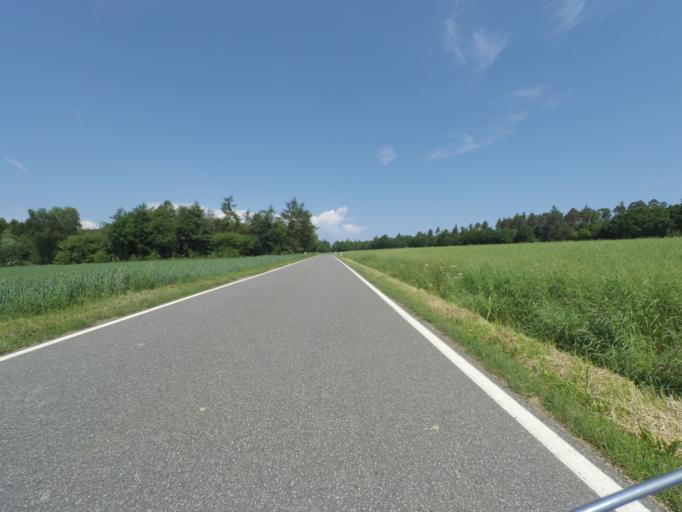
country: DE
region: Rheinland-Pfalz
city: Spesenroth
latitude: 50.0538
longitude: 7.4581
